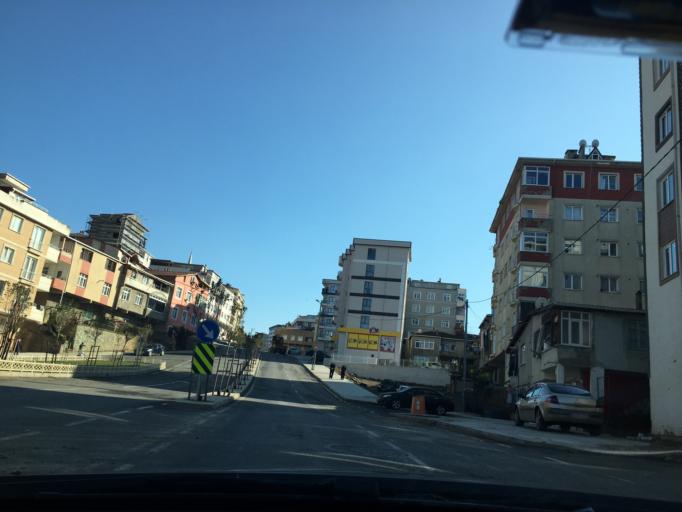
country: TR
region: Istanbul
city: Icmeler
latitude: 40.8697
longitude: 29.3022
